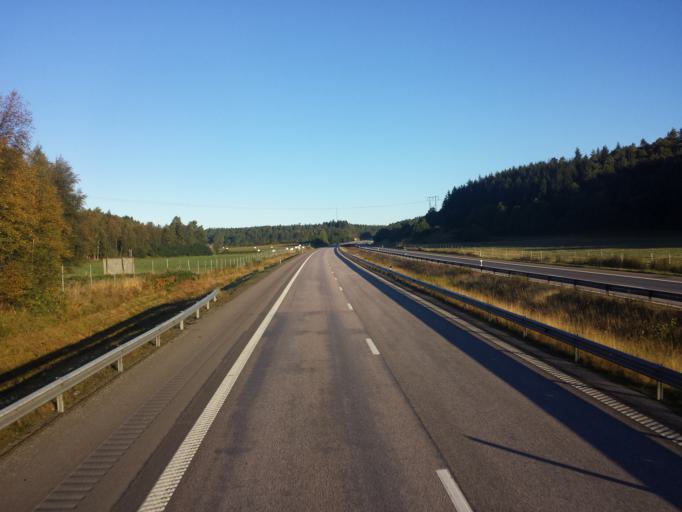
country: SE
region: Halland
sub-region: Varbergs Kommun
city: Varberg
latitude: 57.1813
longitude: 12.2674
